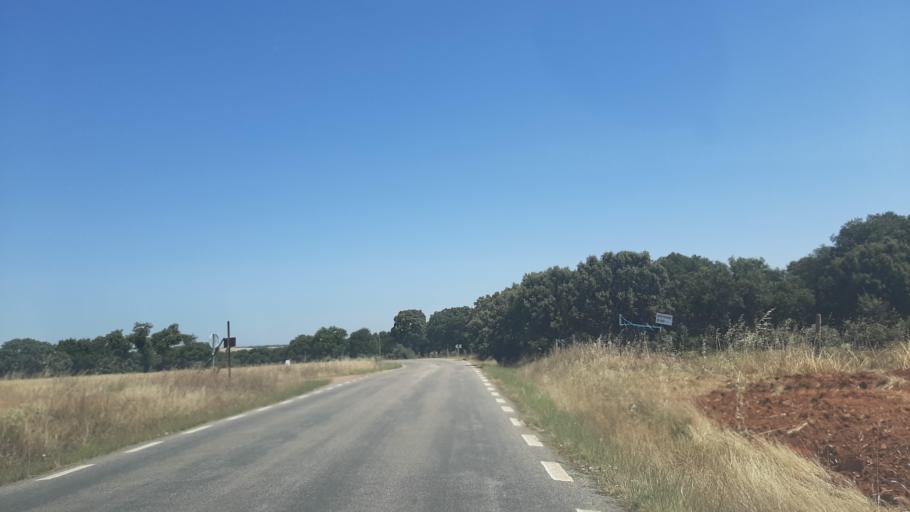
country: ES
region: Castille and Leon
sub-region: Provincia de Salamanca
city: Cabrillas
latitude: 40.7253
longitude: -6.1759
